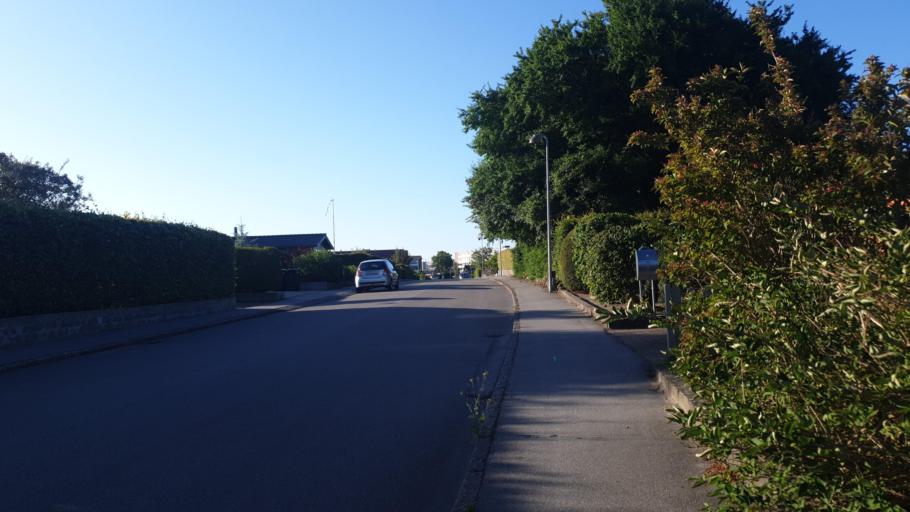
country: DK
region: Zealand
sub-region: Naestved Kommune
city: Naestved
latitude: 55.2271
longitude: 11.7414
